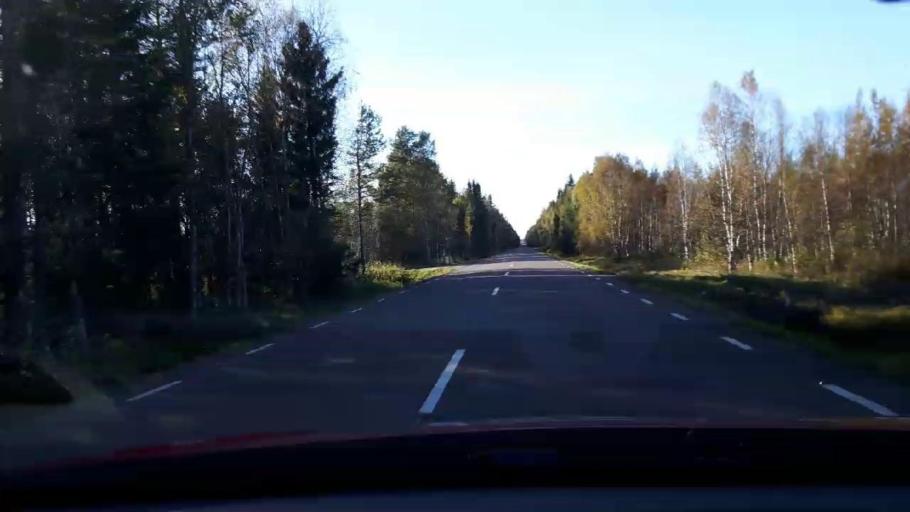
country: SE
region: Jaemtland
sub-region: Stroemsunds Kommun
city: Stroemsund
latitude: 63.8511
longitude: 15.2537
